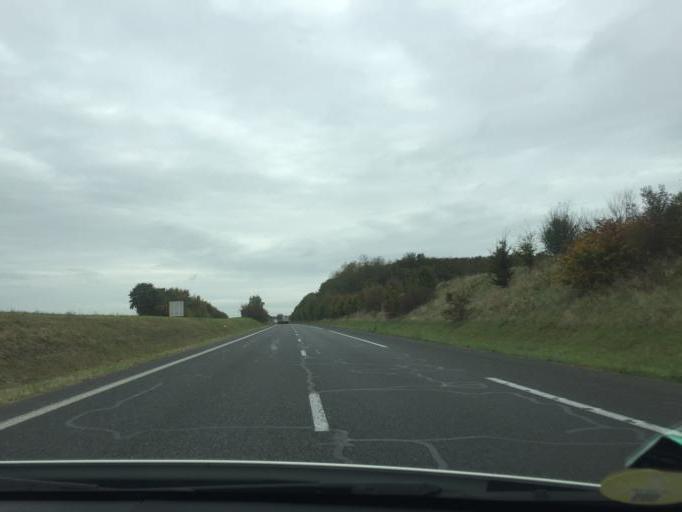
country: FR
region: Bourgogne
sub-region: Departement de l'Yonne
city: Egriselles-le-Bocage
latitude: 48.0767
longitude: 3.1235
